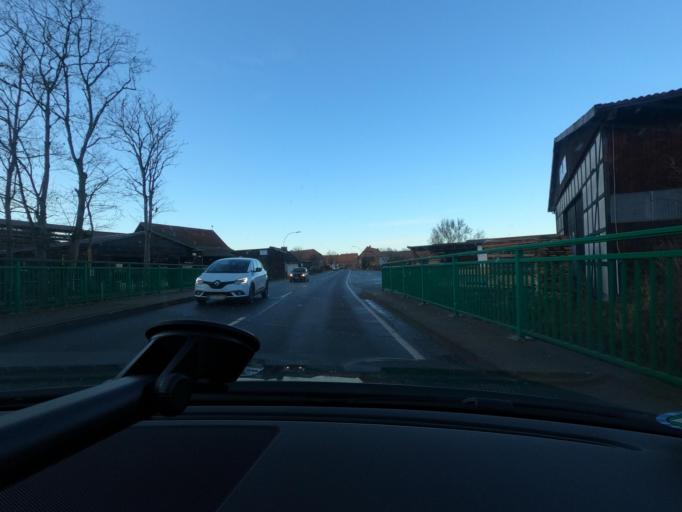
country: DE
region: Lower Saxony
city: Rhumspringe
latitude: 51.6087
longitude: 10.3240
